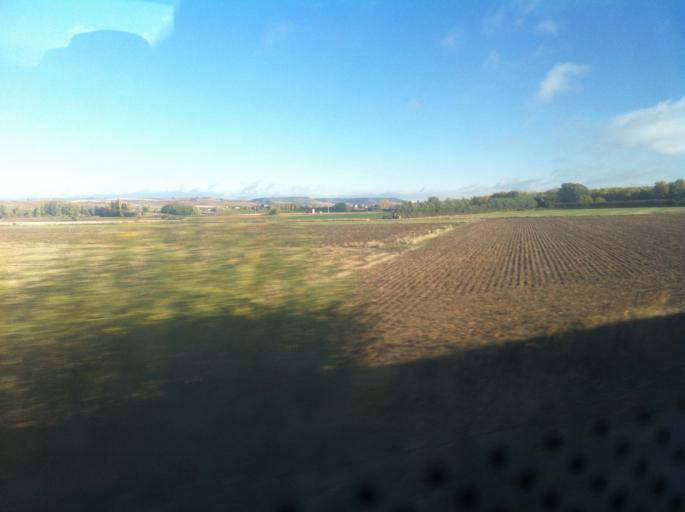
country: ES
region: Castille and Leon
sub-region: Provincia de Palencia
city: Torquemada
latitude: 42.0095
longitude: -4.3375
